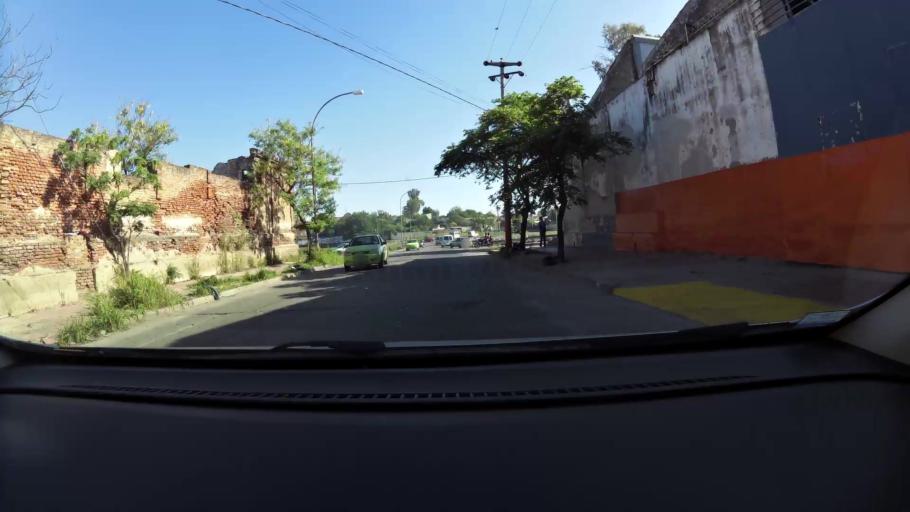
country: AR
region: Cordoba
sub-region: Departamento de Capital
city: Cordoba
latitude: -31.4192
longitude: -64.1501
